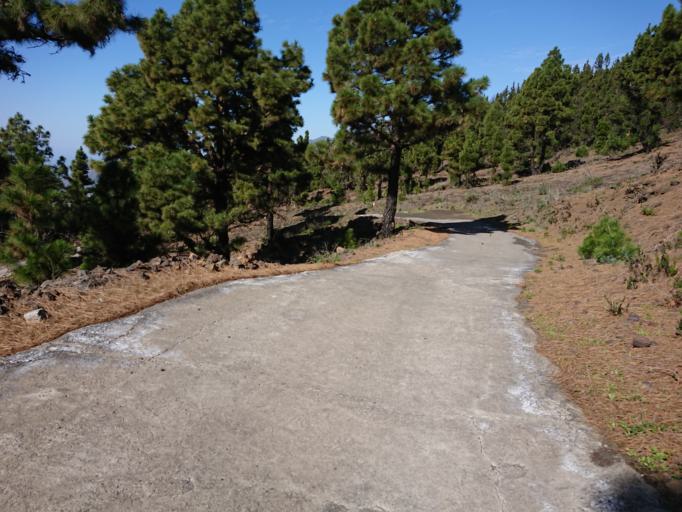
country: ES
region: Canary Islands
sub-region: Provincia de Santa Cruz de Tenerife
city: El Paso
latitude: 28.6076
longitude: -17.8653
